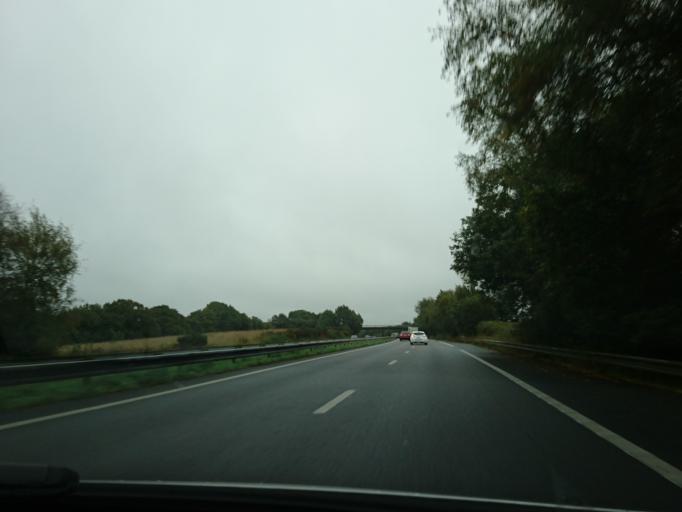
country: FR
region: Brittany
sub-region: Departement du Morbihan
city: Gestel
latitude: 47.7949
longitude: -3.4515
